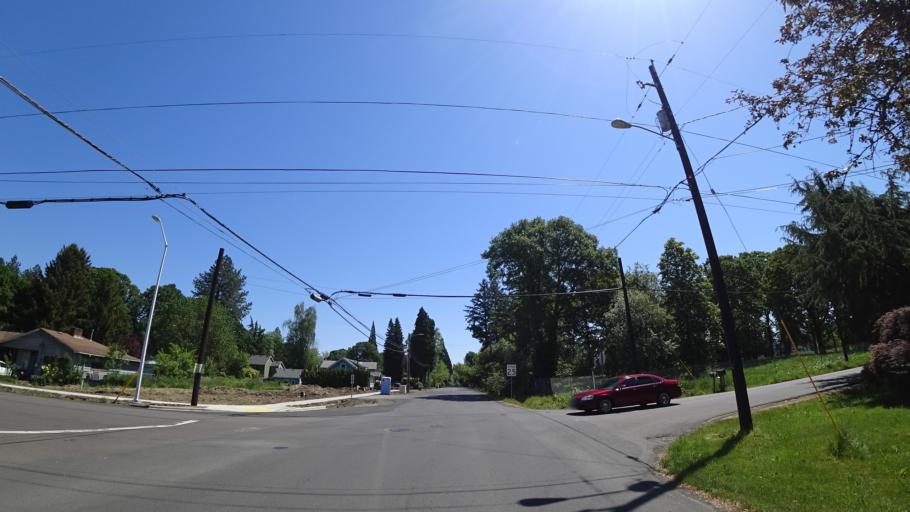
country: US
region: Oregon
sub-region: Washington County
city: Aloha
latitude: 45.4941
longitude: -122.8568
